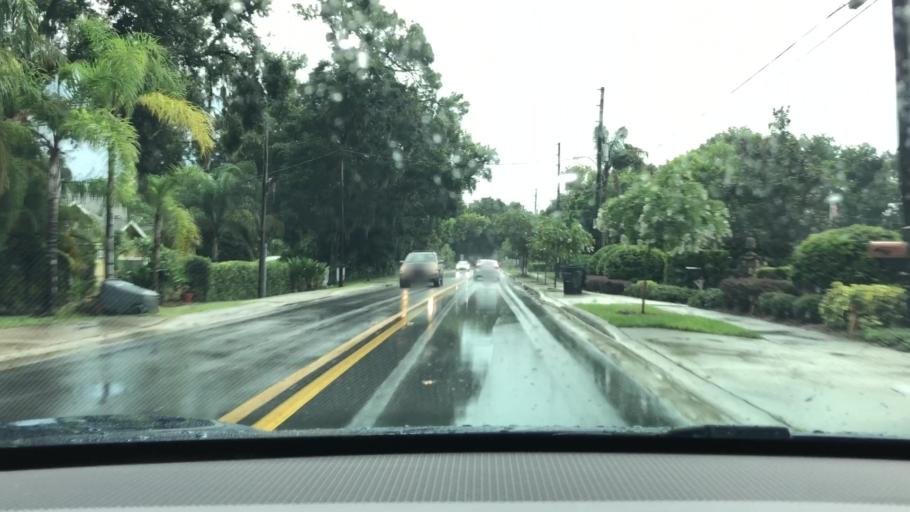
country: US
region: Florida
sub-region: Orange County
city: Edgewood
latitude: 28.4940
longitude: -81.3711
